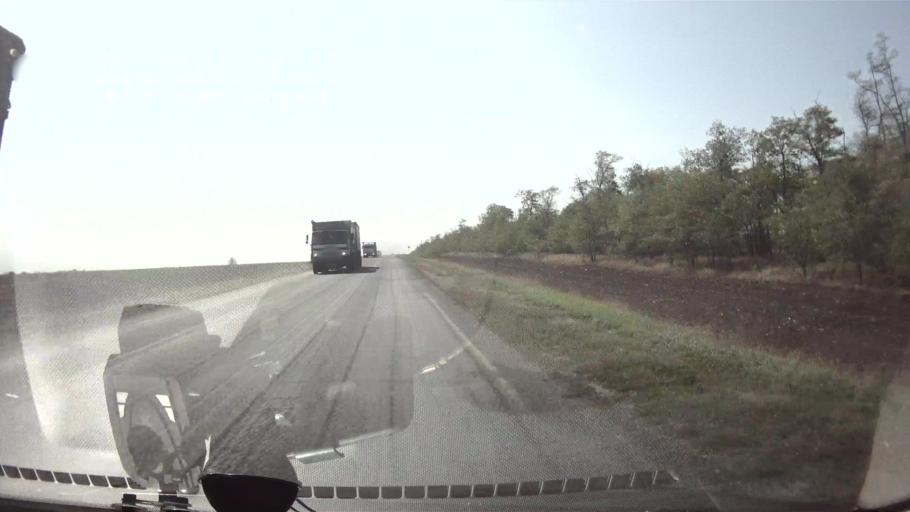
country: RU
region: Krasnodarskiy
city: Dmitriyevskaya
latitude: 45.6873
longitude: 40.7439
